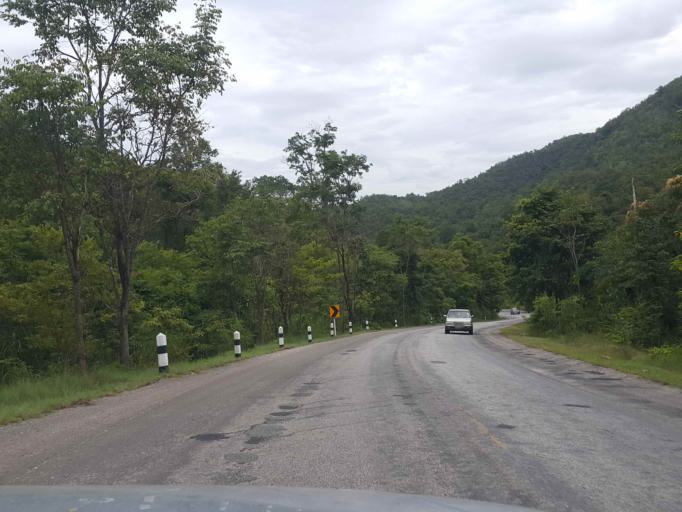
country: TH
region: Lampang
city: Thoen
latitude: 17.6310
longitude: 99.3113
